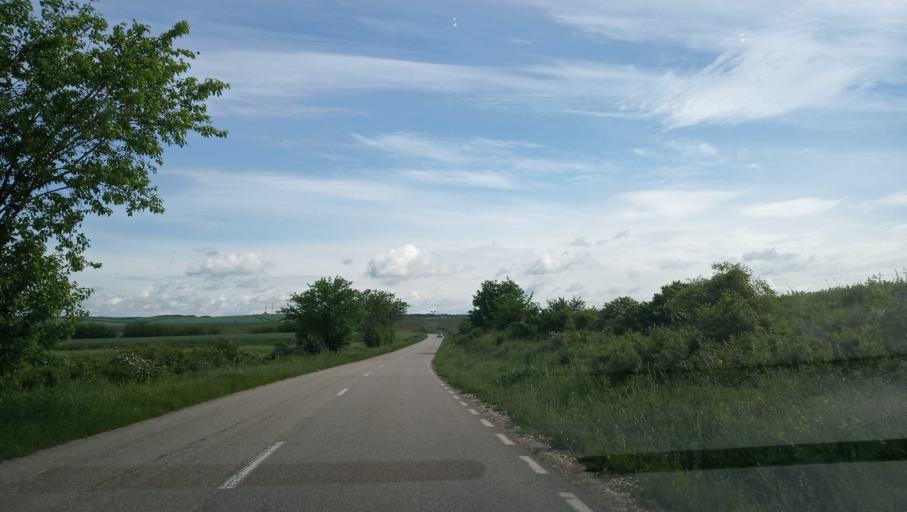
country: RO
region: Timis
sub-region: Comuna Topolovatu Mare
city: Topolovatu Mare
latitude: 45.7892
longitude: 21.6515
